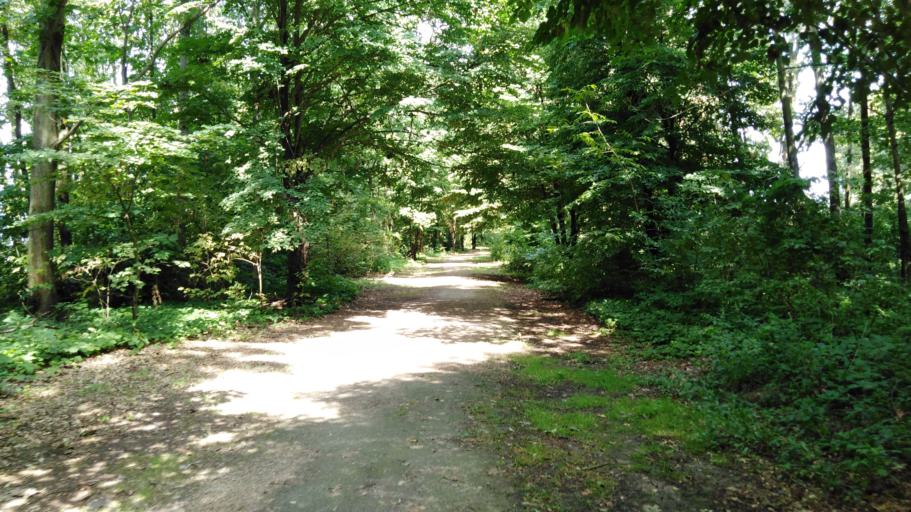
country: HU
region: Zala
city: Zalakomar
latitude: 46.6069
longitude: 17.1667
